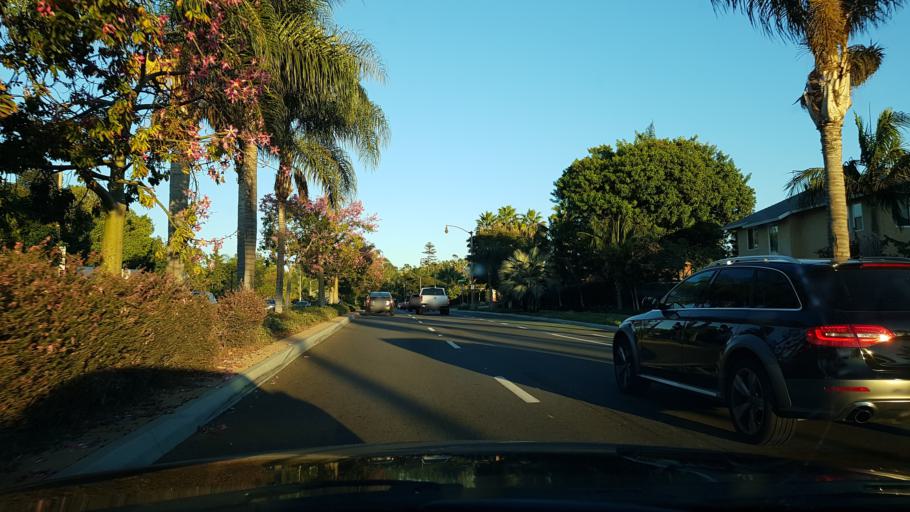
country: US
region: California
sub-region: San Diego County
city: Encinitas
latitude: 33.0651
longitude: -117.2884
